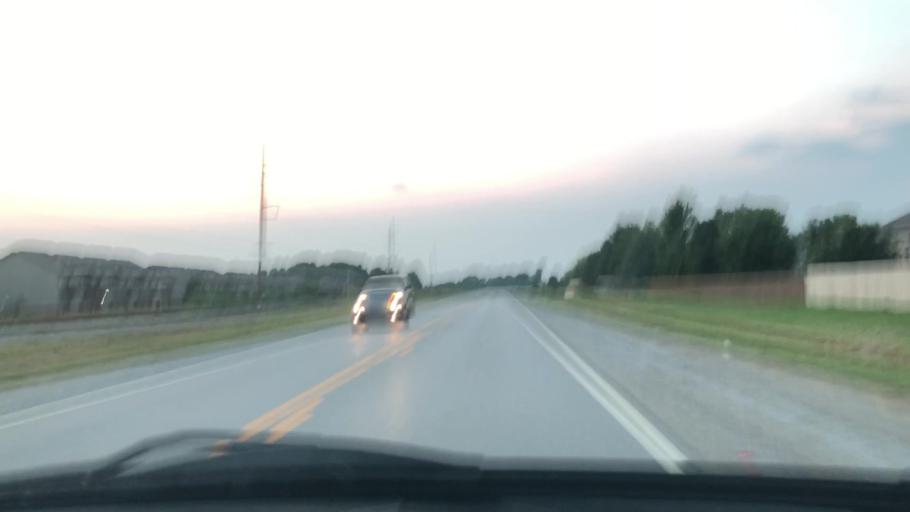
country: US
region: Iowa
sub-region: Johnson County
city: North Liberty
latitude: 41.7633
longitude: -91.6138
